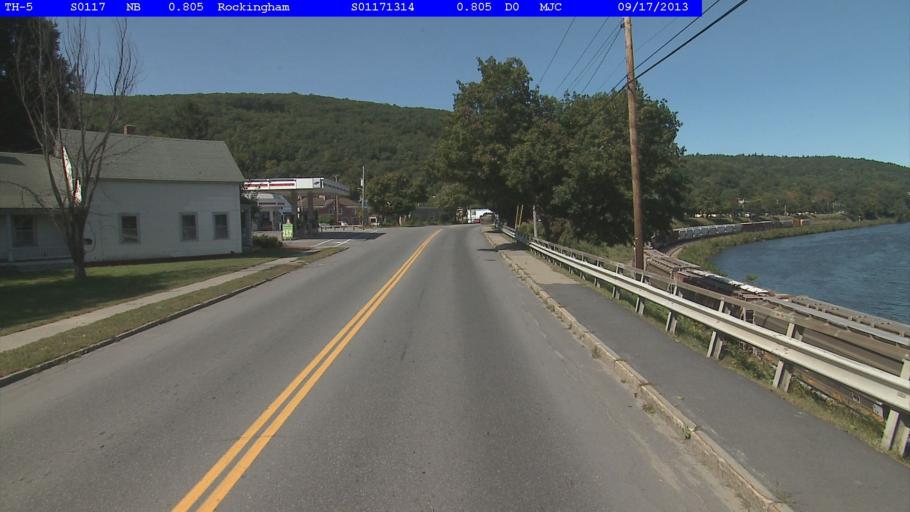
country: US
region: Vermont
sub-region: Windham County
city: Bellows Falls
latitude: 43.1377
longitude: -72.4510
